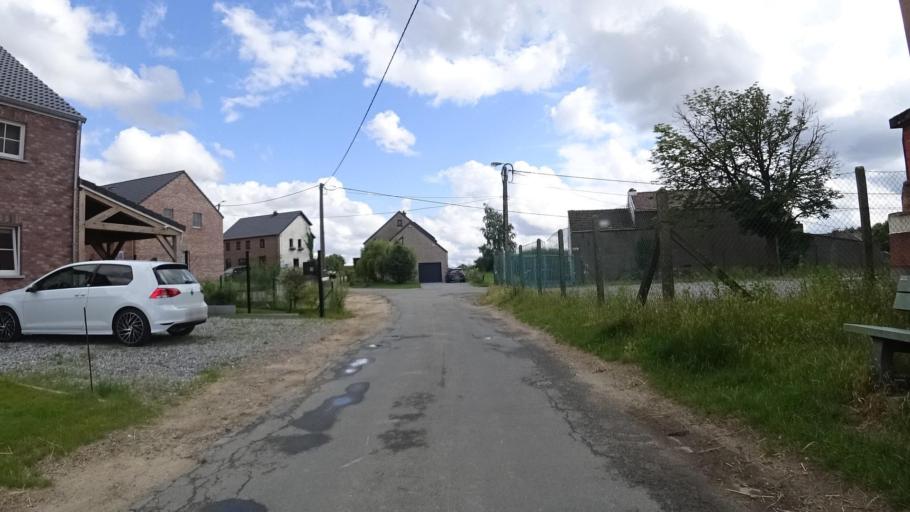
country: BE
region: Wallonia
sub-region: Province du Brabant Wallon
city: Villers-la-Ville
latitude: 50.5604
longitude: 4.5028
